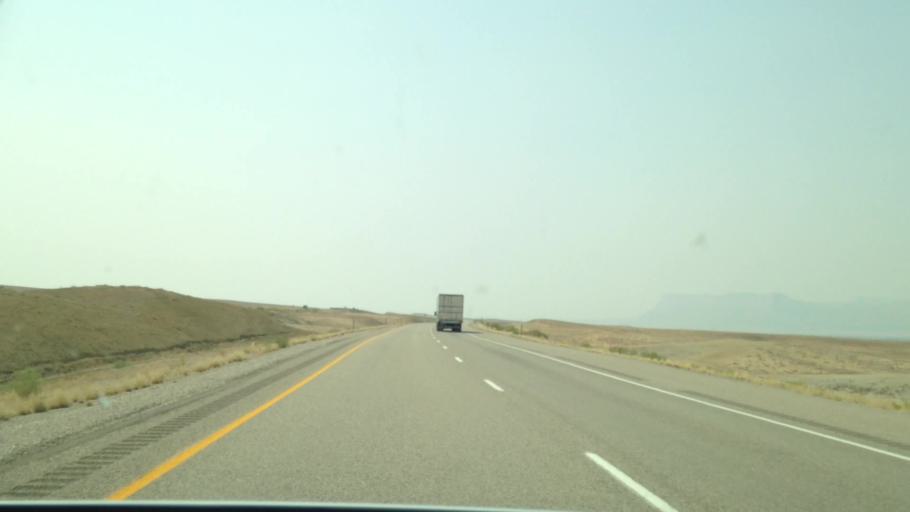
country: US
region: Utah
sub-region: Grand County
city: Moab
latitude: 38.9638
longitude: -110.0724
